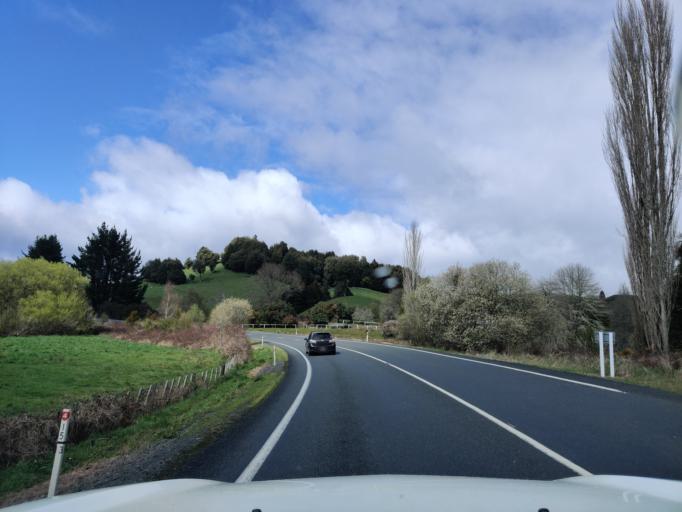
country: NZ
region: Waikato
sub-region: Otorohanga District
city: Otorohanga
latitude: -38.5850
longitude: 175.2152
